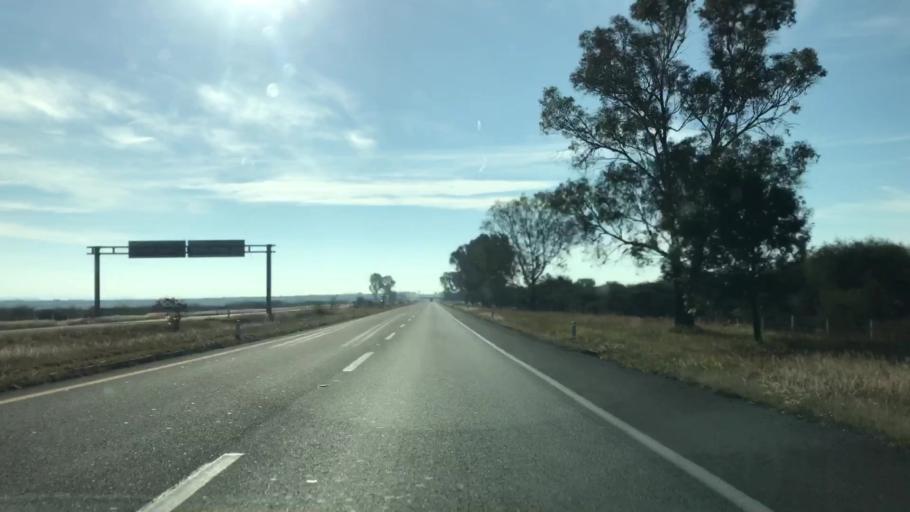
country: MX
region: Jalisco
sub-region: Lagos de Moreno
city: Cristeros [Fraccionamiento]
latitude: 21.2472
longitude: -101.9445
